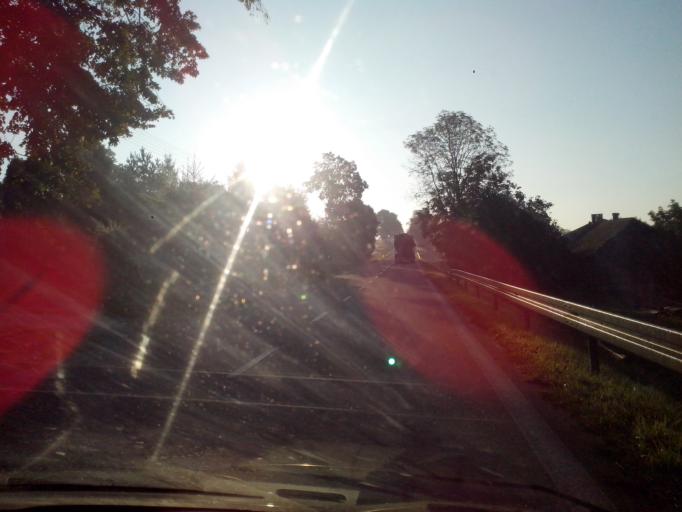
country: PL
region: Subcarpathian Voivodeship
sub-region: Powiat brzozowski
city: Wesola
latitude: 49.8357
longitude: 22.1456
